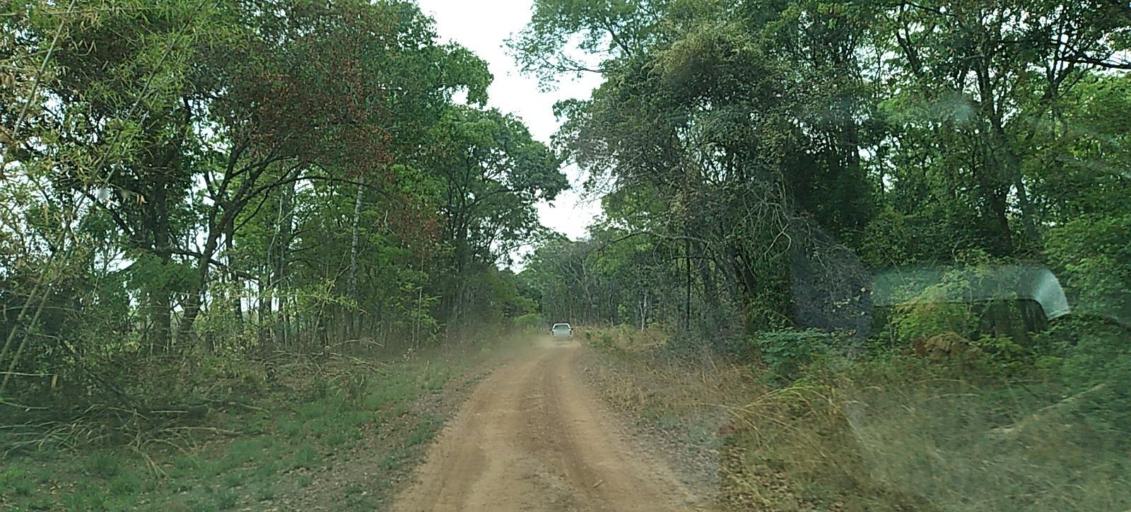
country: ZM
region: Copperbelt
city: Chingola
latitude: -12.7945
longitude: 27.6436
